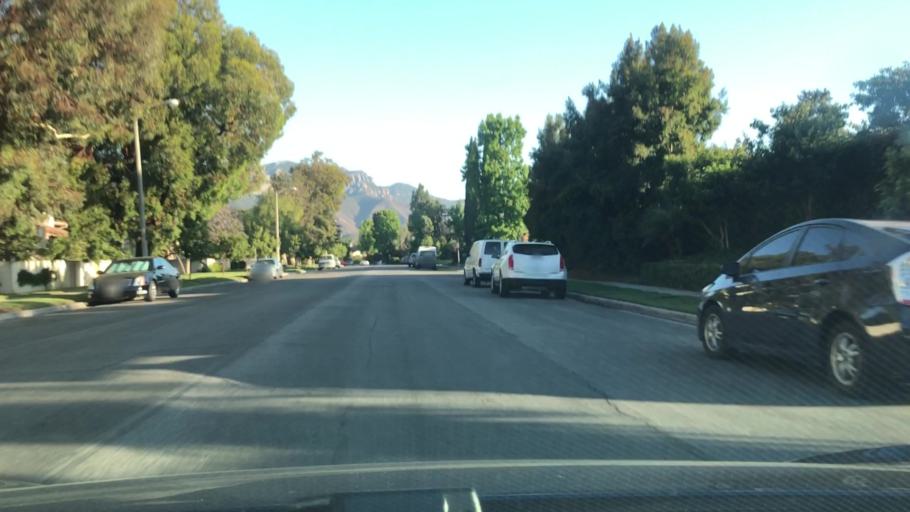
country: US
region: California
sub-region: Ventura County
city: Casa Conejo
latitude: 34.1814
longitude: -118.9556
